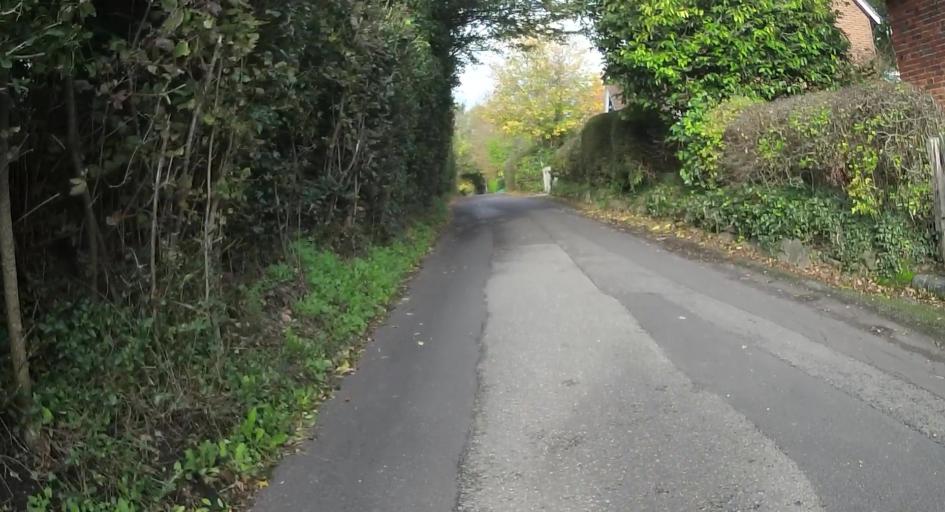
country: GB
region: England
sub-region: Hampshire
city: Old Basing
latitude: 51.2829
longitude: -1.0502
